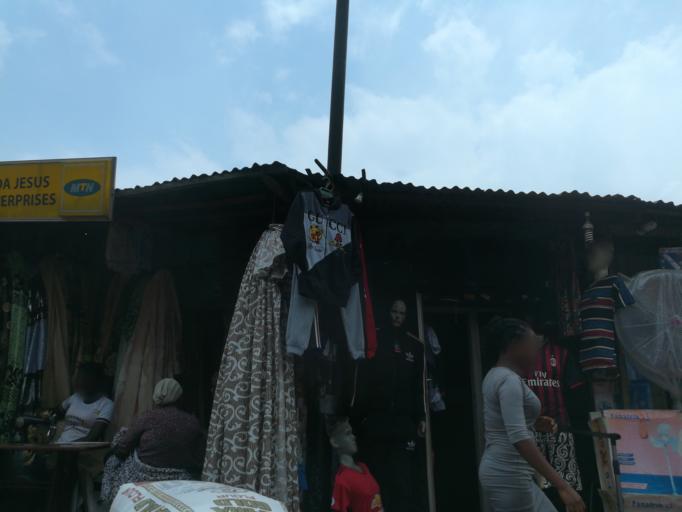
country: NG
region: Lagos
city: Agege
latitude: 6.6225
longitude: 3.3244
